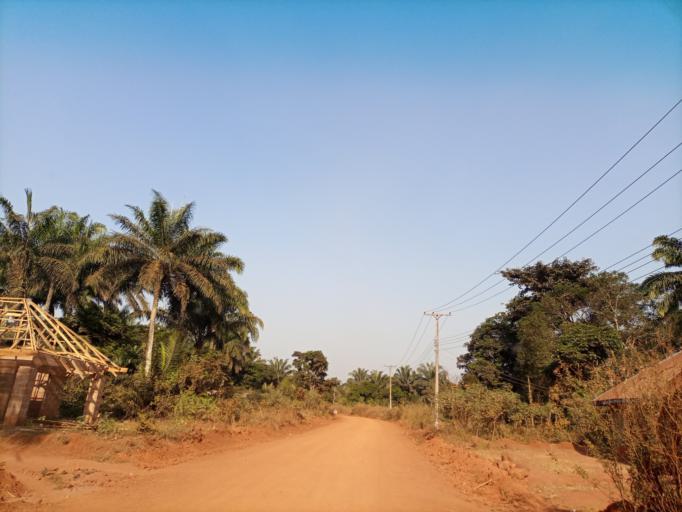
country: NG
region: Enugu
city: Opi
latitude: 6.7770
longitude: 7.3862
